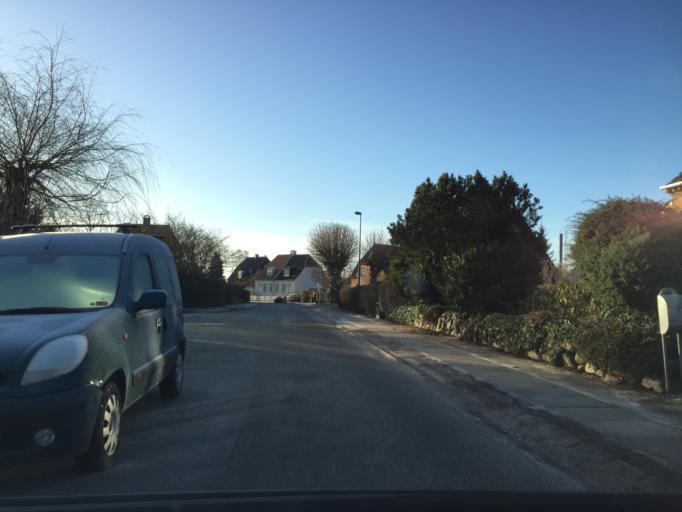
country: DK
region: Capital Region
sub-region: Kobenhavn
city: Vanlose
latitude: 55.6621
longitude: 12.4968
